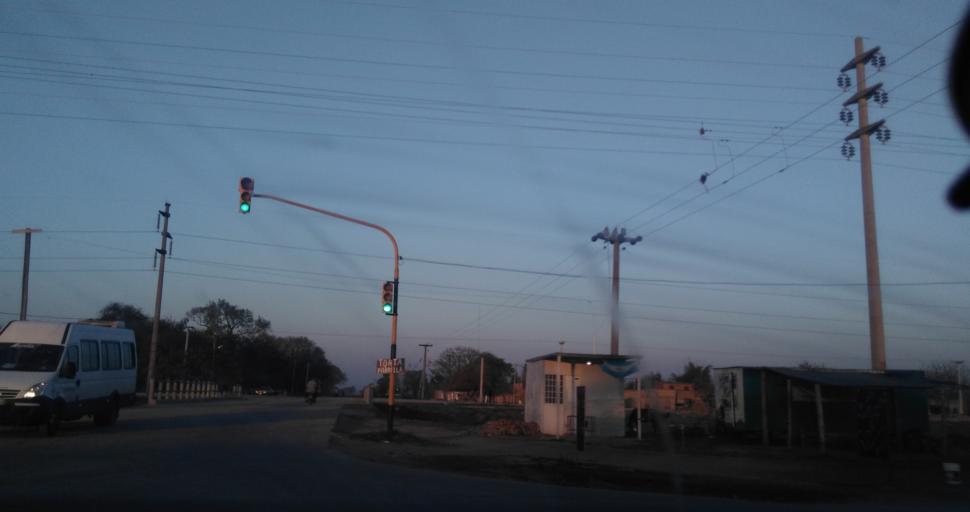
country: AR
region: Chaco
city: Resistencia
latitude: -27.4895
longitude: -58.9864
